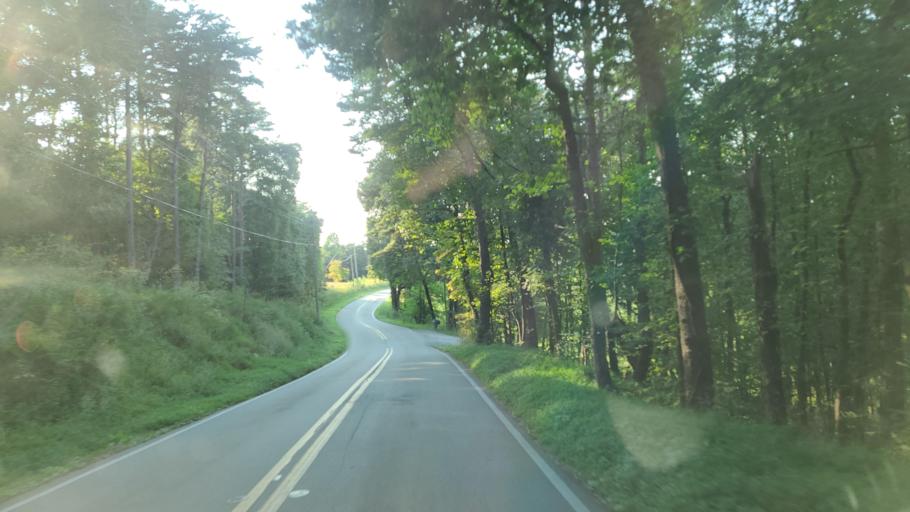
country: US
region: Georgia
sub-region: Pickens County
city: Jasper
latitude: 34.4251
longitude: -84.5430
